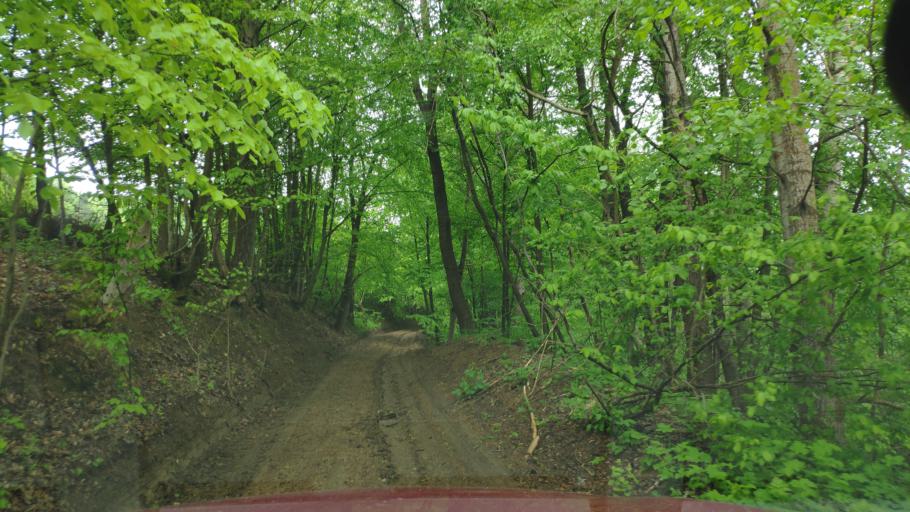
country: SK
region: Presovsky
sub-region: Okres Presov
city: Presov
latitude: 48.9312
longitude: 21.1662
